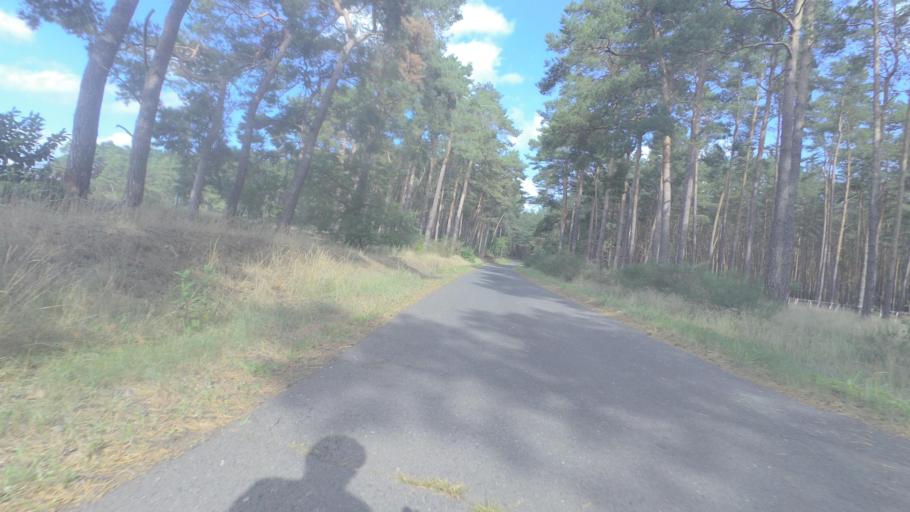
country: DE
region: Brandenburg
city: Munchehofe
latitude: 52.1657
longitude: 13.8807
